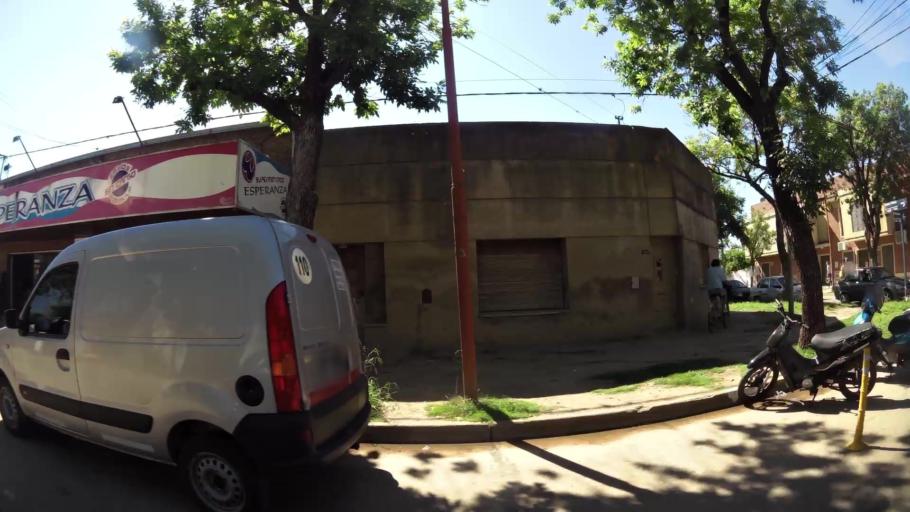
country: AR
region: Santa Fe
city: Esperanza
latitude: -31.4551
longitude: -60.9343
